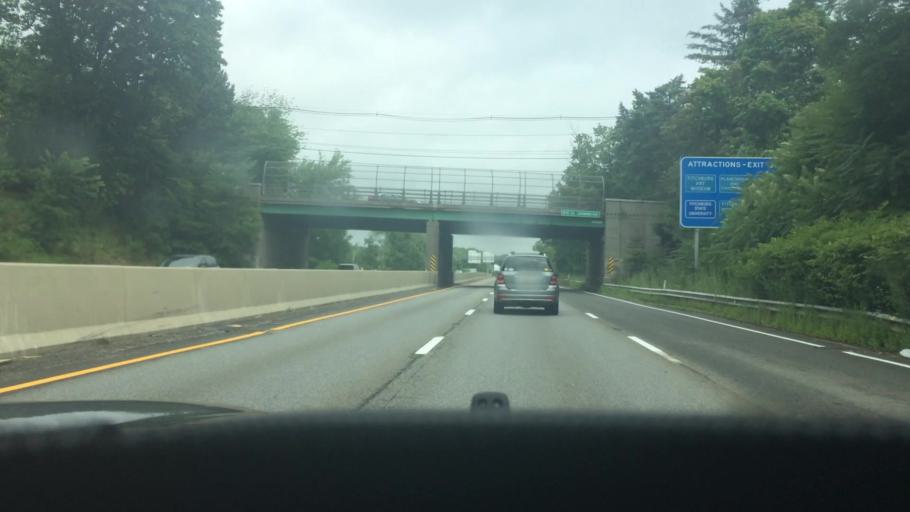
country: US
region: Massachusetts
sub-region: Worcester County
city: Leominster
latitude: 42.5371
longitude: -71.7432
